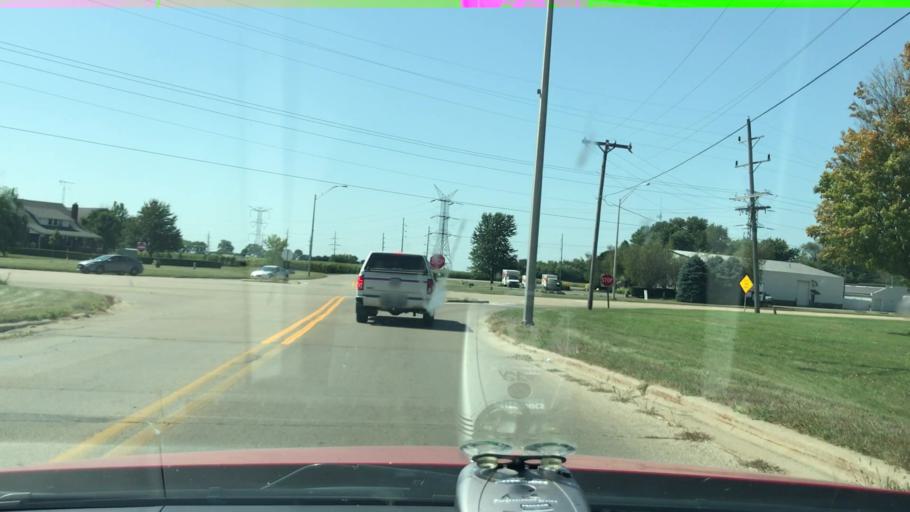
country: US
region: Illinois
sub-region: Whiteside County
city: Sterling
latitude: 41.7729
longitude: -89.7163
